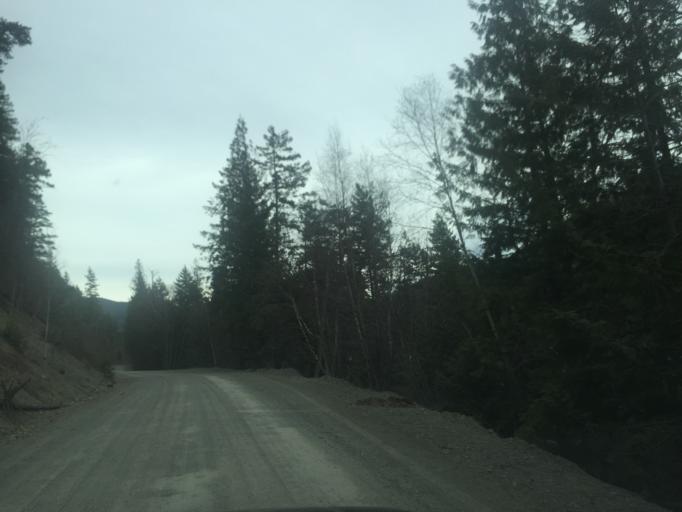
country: CA
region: British Columbia
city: Chase
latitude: 51.4289
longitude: -120.1356
